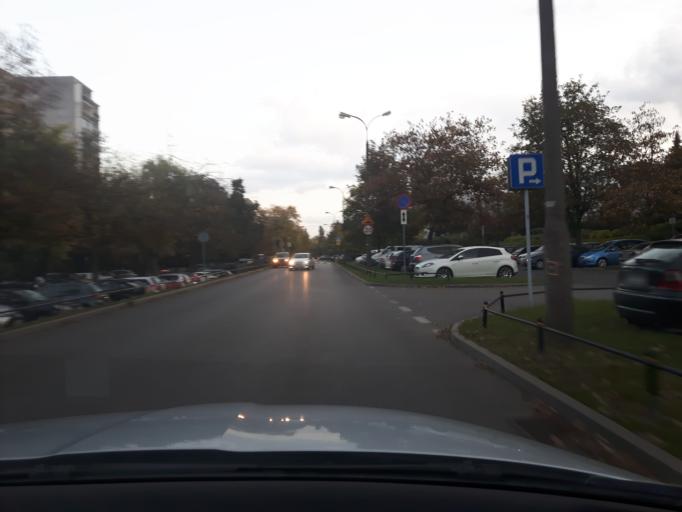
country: PL
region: Masovian Voivodeship
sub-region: Warszawa
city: Ursynow
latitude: 52.1417
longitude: 21.0507
